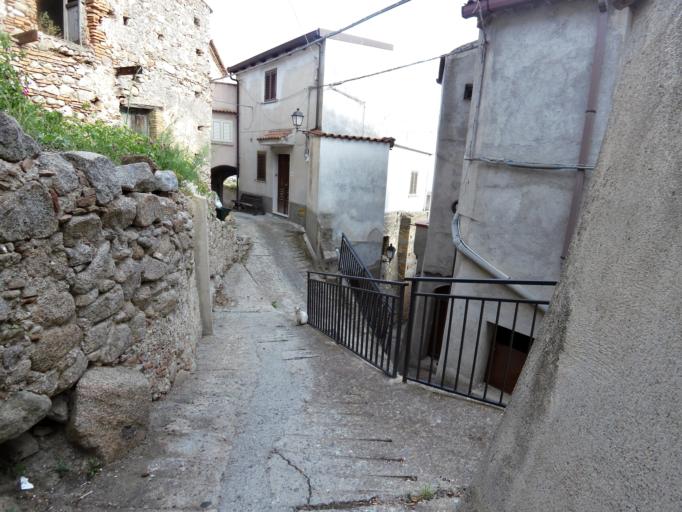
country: IT
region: Calabria
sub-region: Provincia di Reggio Calabria
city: Stignano
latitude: 38.4165
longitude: 16.4719
